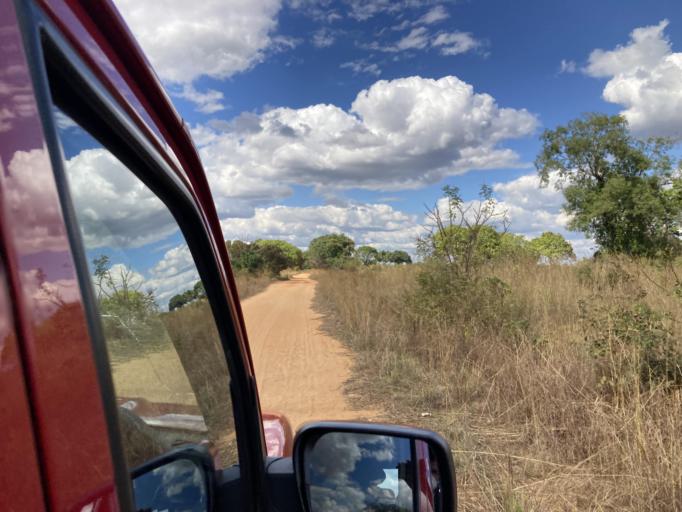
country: MZ
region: Cabo Delgado
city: Montepuez
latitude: -13.1260
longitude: 39.0432
